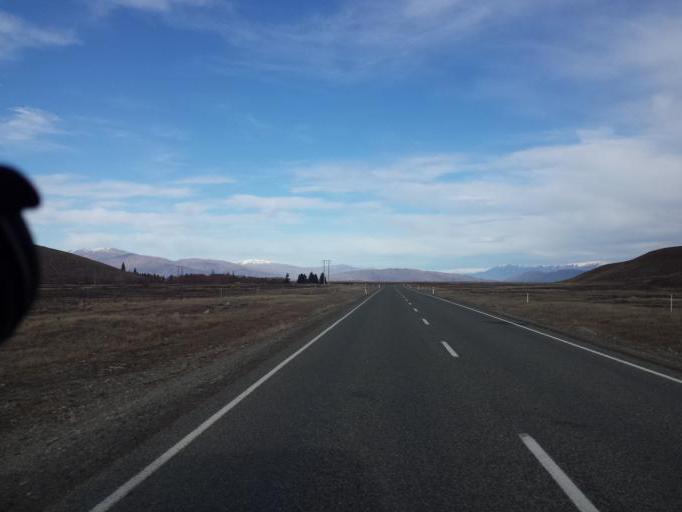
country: NZ
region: Canterbury
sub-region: Timaru District
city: Pleasant Point
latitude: -44.0503
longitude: 170.5041
